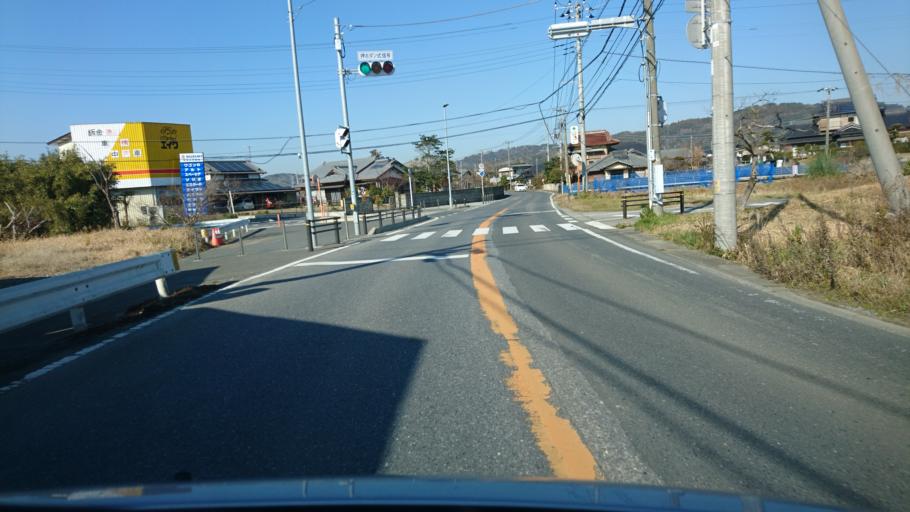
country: JP
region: Chiba
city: Kimitsu
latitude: 35.2998
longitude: 139.9752
